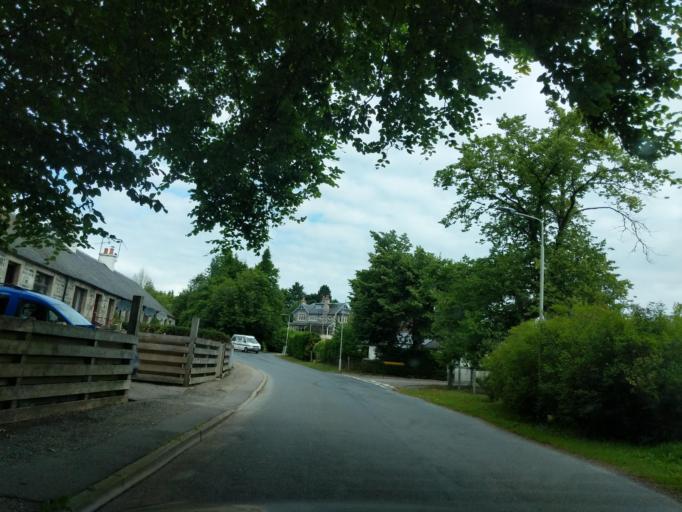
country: GB
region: Scotland
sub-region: Highland
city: Grantown on Spey
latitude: 57.3272
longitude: -3.6144
